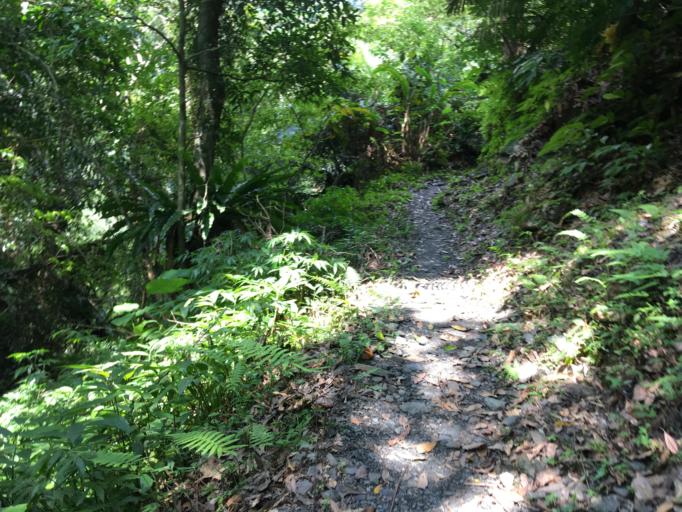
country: TW
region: Taiwan
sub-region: Yilan
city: Yilan
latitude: 24.4223
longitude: 121.6958
